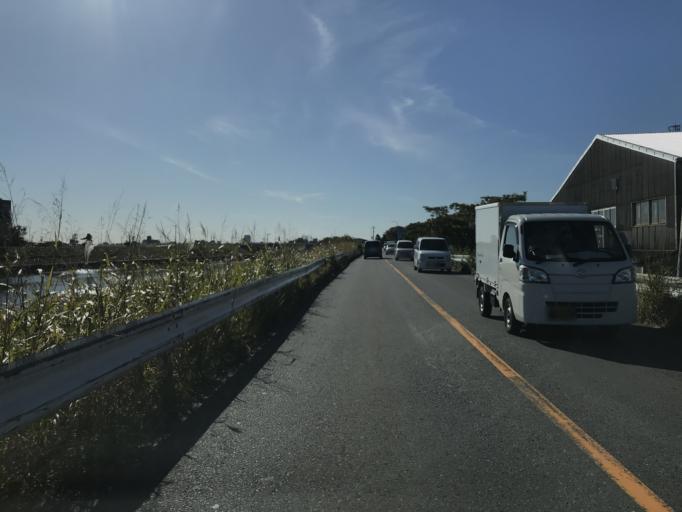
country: JP
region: Aichi
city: Nagoya-shi
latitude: 35.1851
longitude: 136.8442
